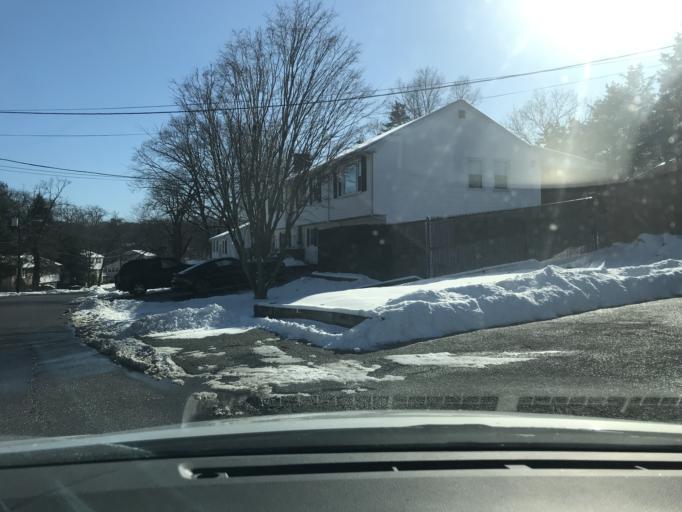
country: US
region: Massachusetts
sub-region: Essex County
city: Saugus
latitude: 42.4743
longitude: -71.0073
